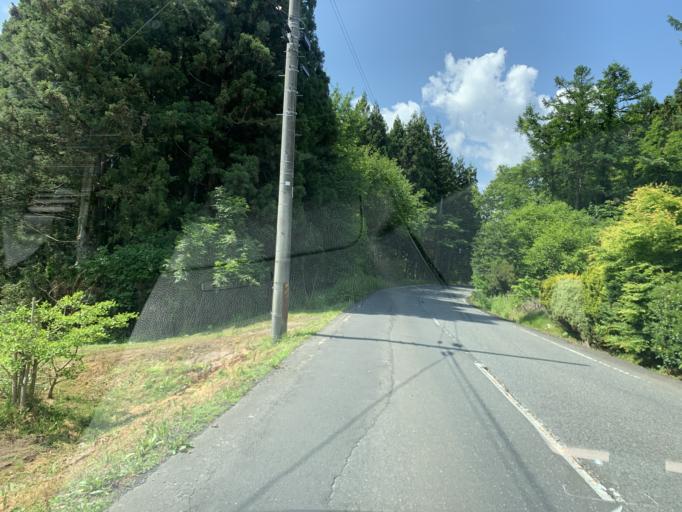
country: JP
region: Miyagi
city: Furukawa
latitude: 38.7173
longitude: 140.9483
